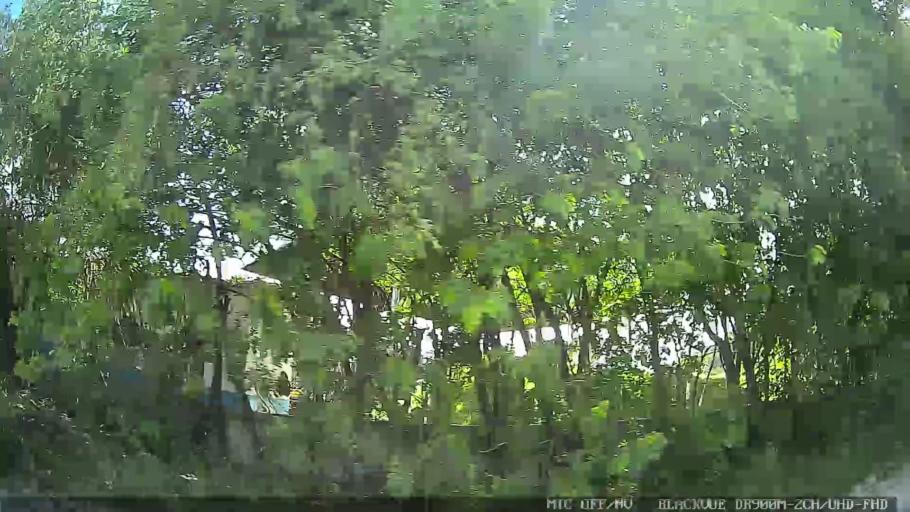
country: BR
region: Sao Paulo
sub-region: Caraguatatuba
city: Caraguatatuba
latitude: -23.6343
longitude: -45.4440
